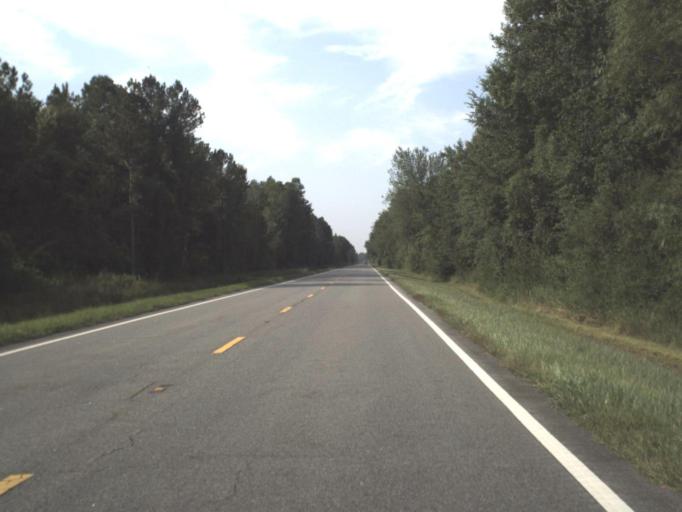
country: US
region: Florida
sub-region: Taylor County
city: Perry
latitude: 30.3172
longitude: -83.6403
